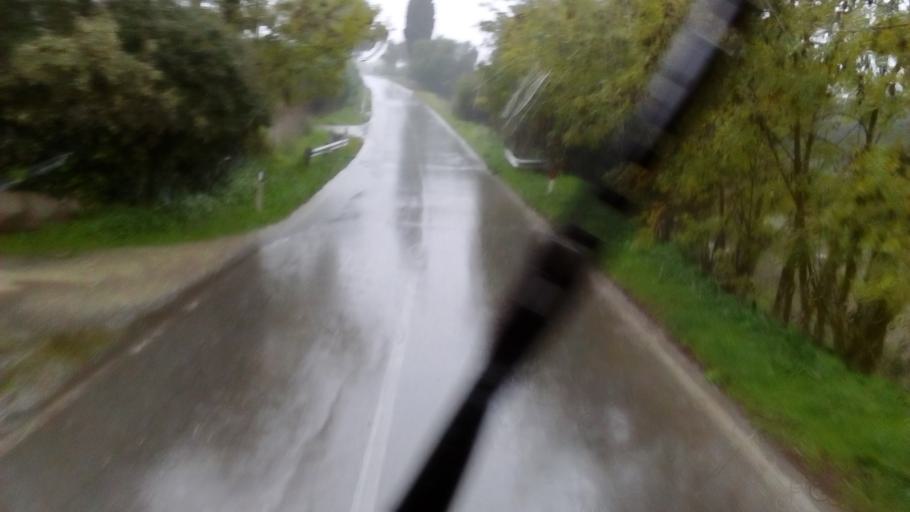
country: IT
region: Sicily
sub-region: Enna
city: Pietraperzia
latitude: 37.4212
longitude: 14.1621
